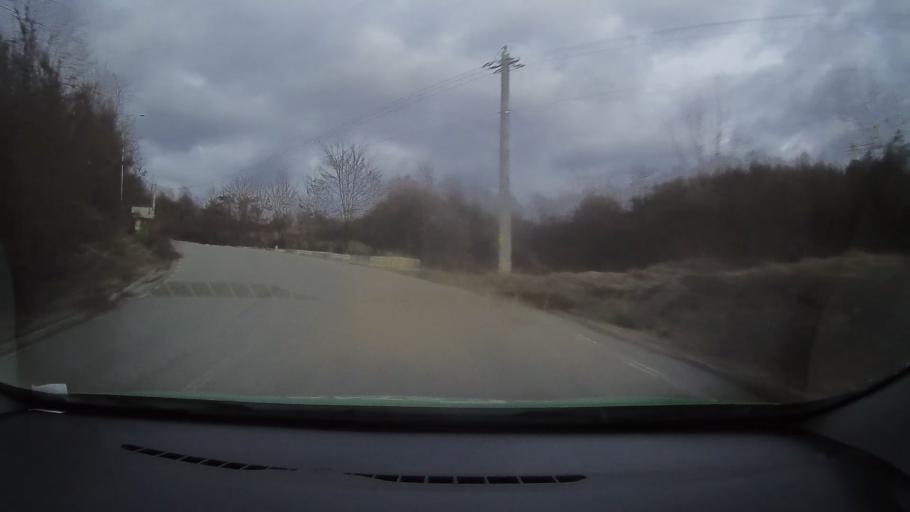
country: RO
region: Prahova
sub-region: Comuna Adunati
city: Adunati
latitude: 45.1305
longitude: 25.6128
